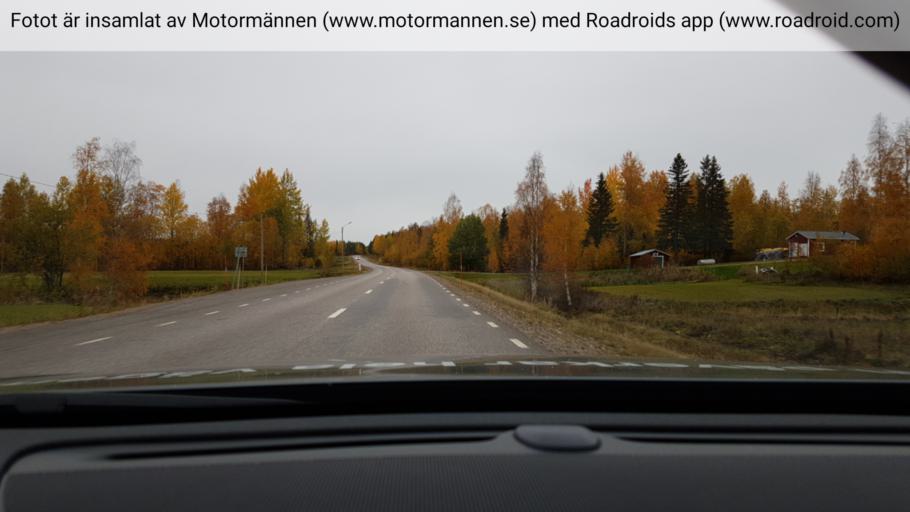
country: SE
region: Norrbotten
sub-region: Overkalix Kommun
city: OEverkalix
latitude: 66.5667
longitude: 22.7615
